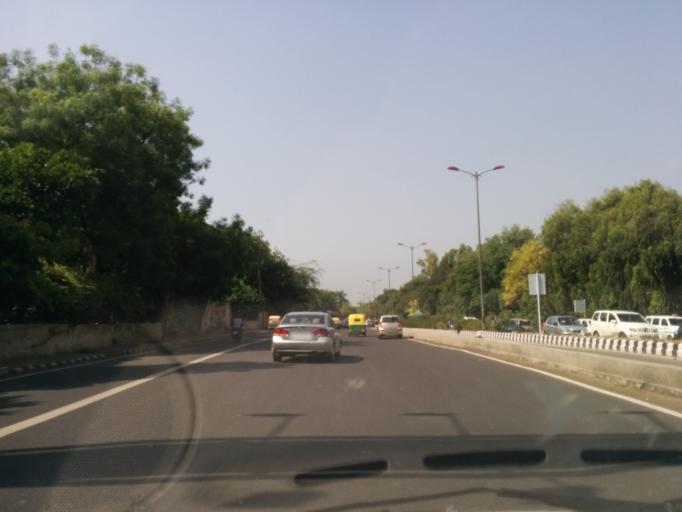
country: IN
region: NCT
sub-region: New Delhi
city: New Delhi
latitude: 28.5555
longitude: 77.2062
